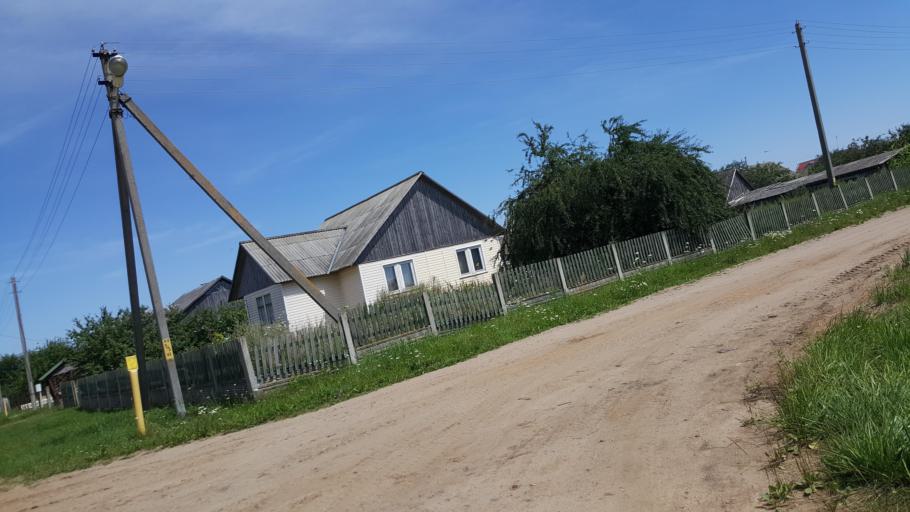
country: BY
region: Brest
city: Pruzhany
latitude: 52.5533
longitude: 24.2005
